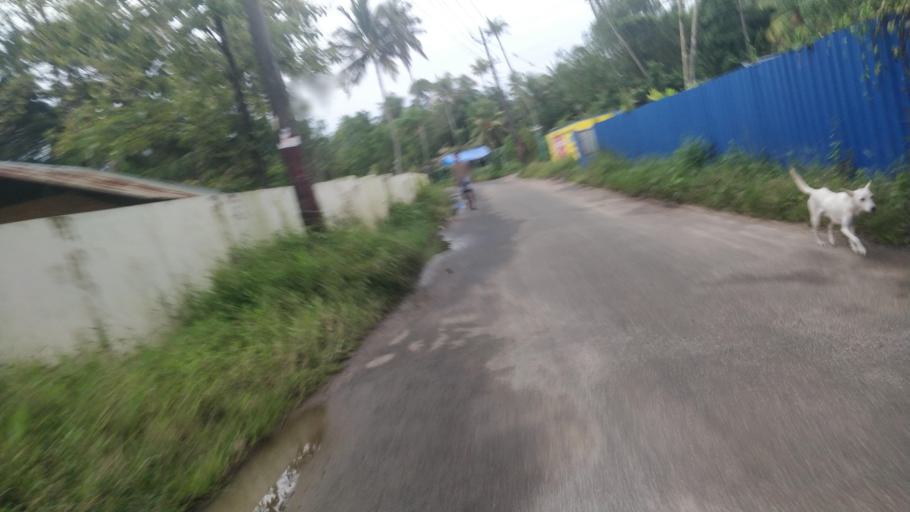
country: IN
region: Kerala
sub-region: Alappuzha
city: Vayalar
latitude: 9.7024
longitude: 76.3481
